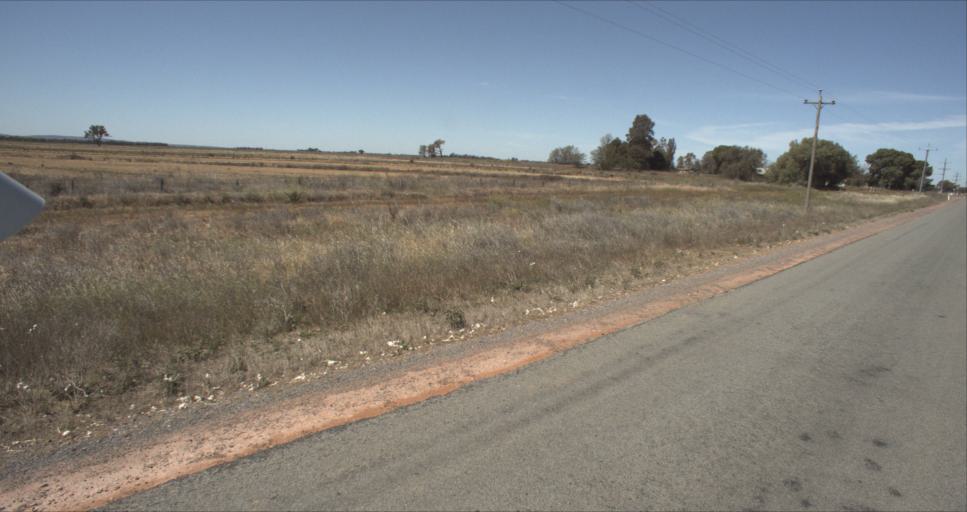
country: AU
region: New South Wales
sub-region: Leeton
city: Leeton
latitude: -34.4390
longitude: 146.2982
